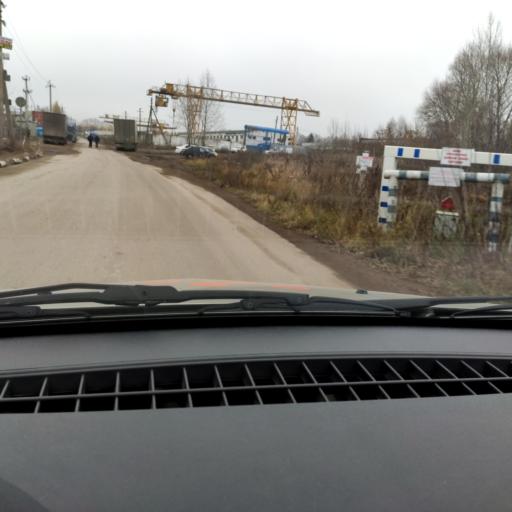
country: RU
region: Bashkortostan
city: Ufa
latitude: 54.5796
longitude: 55.8954
